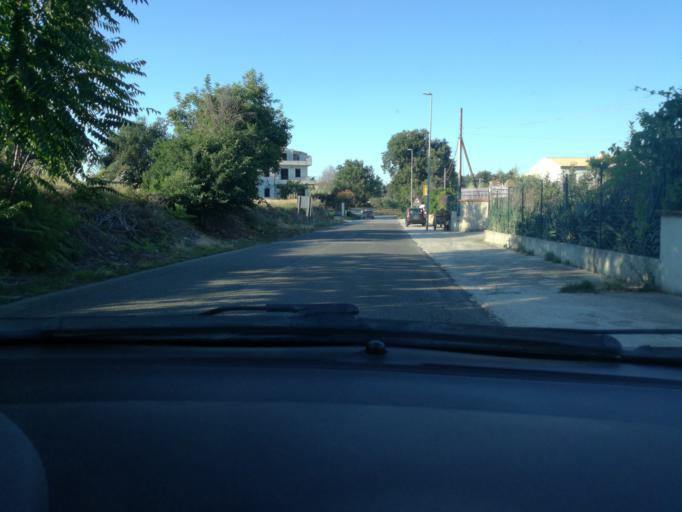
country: IT
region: Molise
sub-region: Provincia di Campobasso
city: Guglionesi
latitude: 41.9247
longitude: 14.9206
